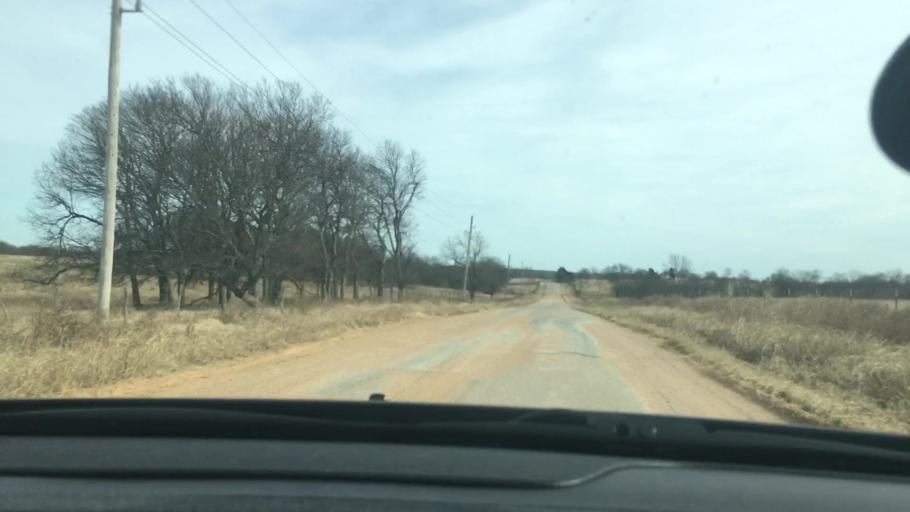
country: US
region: Oklahoma
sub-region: Murray County
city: Sulphur
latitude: 34.4050
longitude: -96.8899
